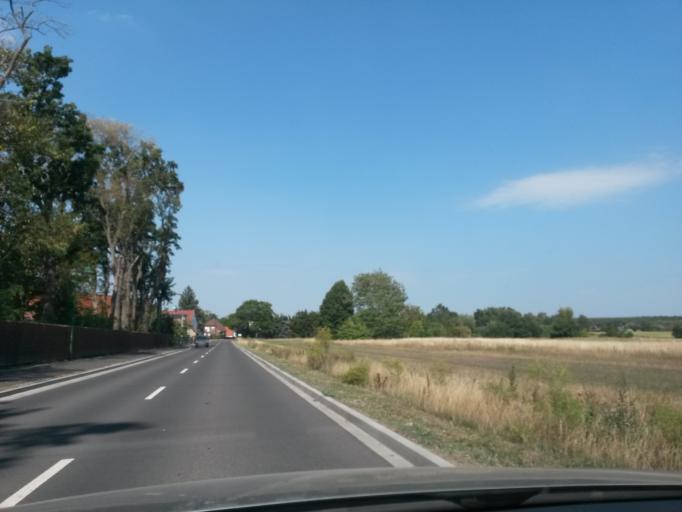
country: DE
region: Saxony-Anhalt
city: Jerichow
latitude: 52.4339
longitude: 11.9974
